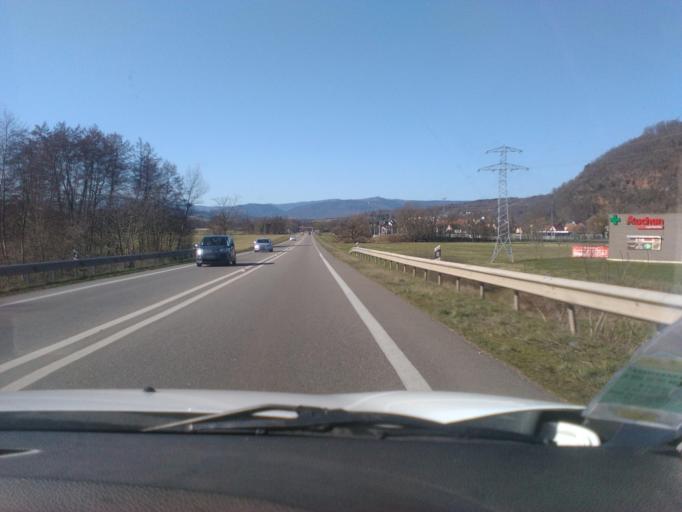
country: FR
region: Alsace
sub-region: Departement du Bas-Rhin
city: Mutzig
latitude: 48.5347
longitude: 7.4477
